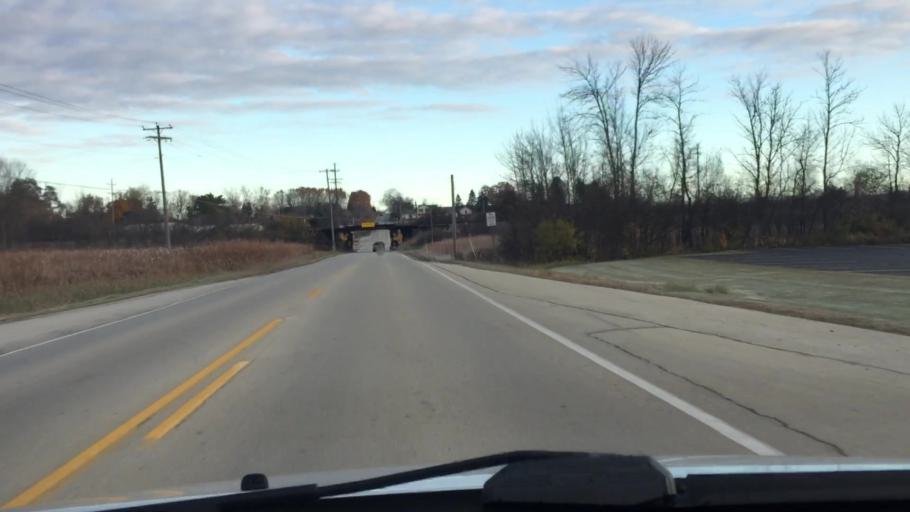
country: US
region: Wisconsin
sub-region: Waukesha County
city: Okauchee Lake
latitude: 43.1755
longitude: -88.4589
